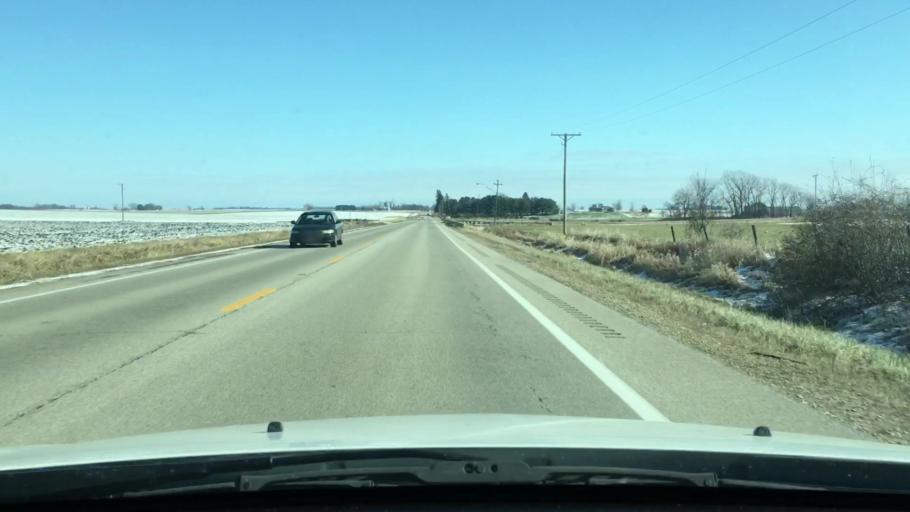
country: US
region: Illinois
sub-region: DeKalb County
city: Malta
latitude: 42.0010
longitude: -88.8607
